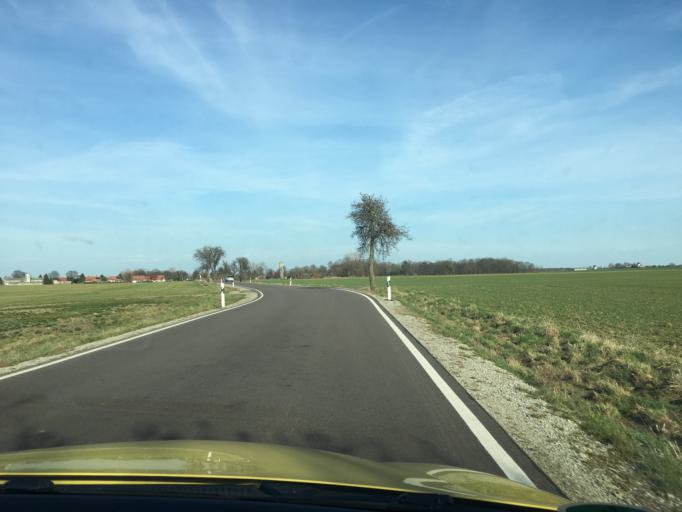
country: DE
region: Saxony-Anhalt
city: Gleina
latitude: 51.2603
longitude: 11.7415
